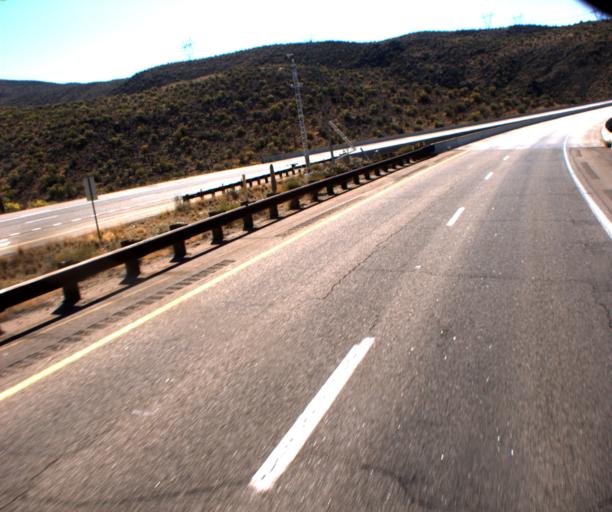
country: US
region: Arizona
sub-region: Yavapai County
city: Bagdad
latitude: 34.5799
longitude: -113.4931
